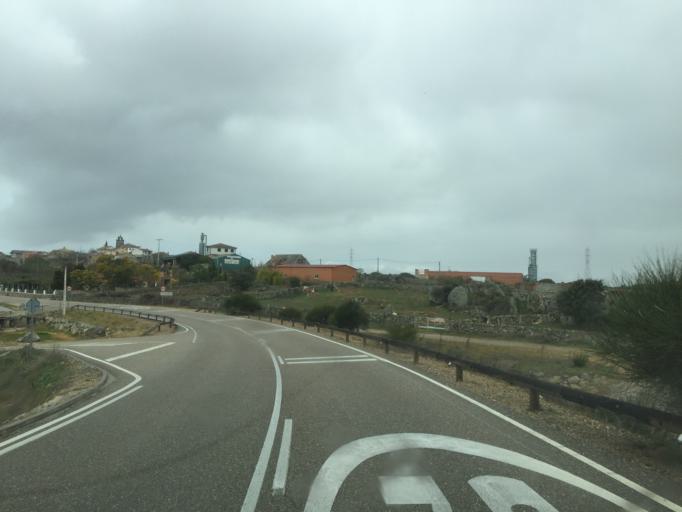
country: ES
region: Castille and Leon
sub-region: Provincia de Zamora
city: Villalcampo
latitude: 41.5251
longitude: -6.0378
